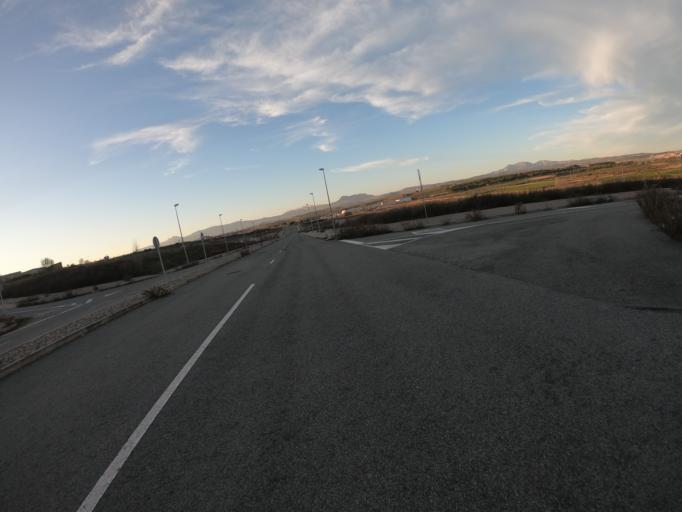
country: ES
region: Basque Country
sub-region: Provincia de Alava
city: Oyon
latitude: 42.4822
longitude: -2.4135
